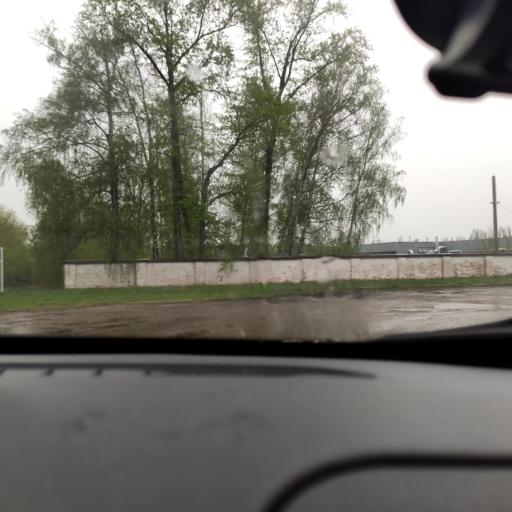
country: RU
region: Voronezj
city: Maslovka
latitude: 51.5380
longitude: 39.3464
